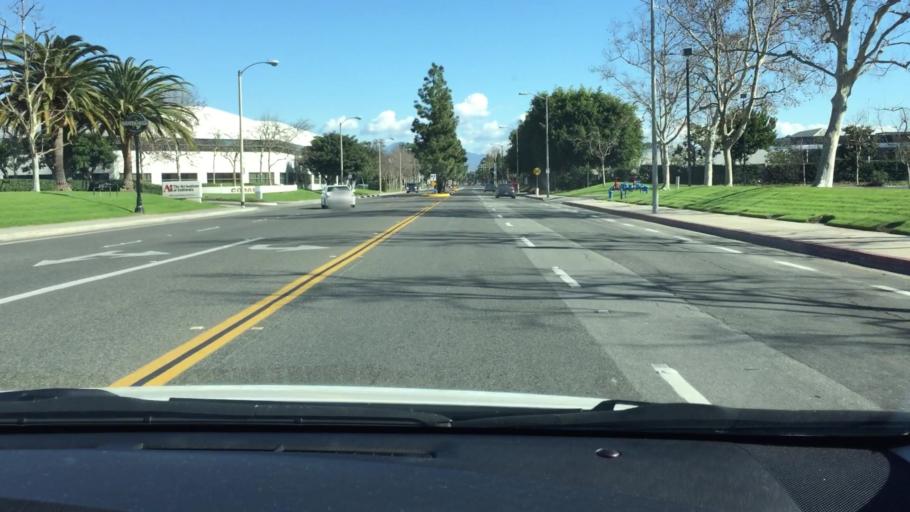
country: US
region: California
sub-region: Orange County
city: Fountain Valley
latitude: 33.6956
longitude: -117.9185
